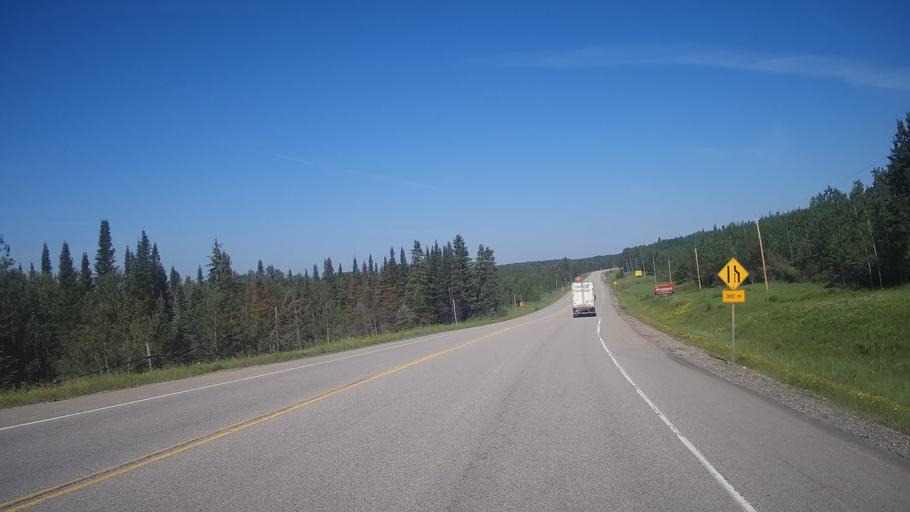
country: CA
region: Ontario
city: Dryden
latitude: 49.6926
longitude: -92.5381
